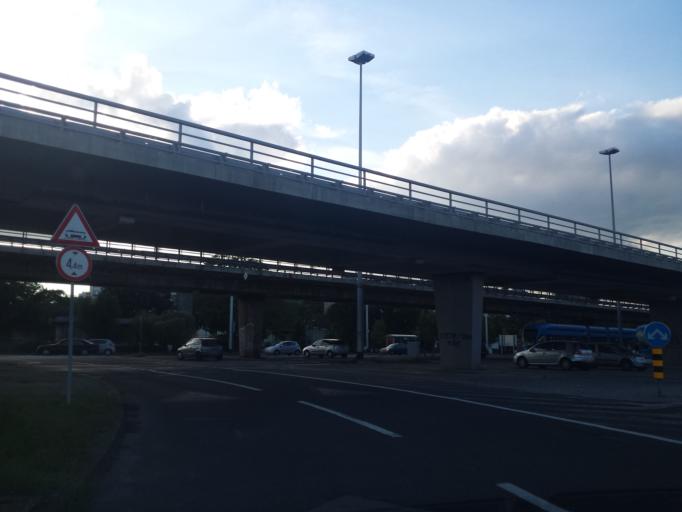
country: HR
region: Grad Zagreb
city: Novi Zagreb
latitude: 45.7786
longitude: 16.0024
